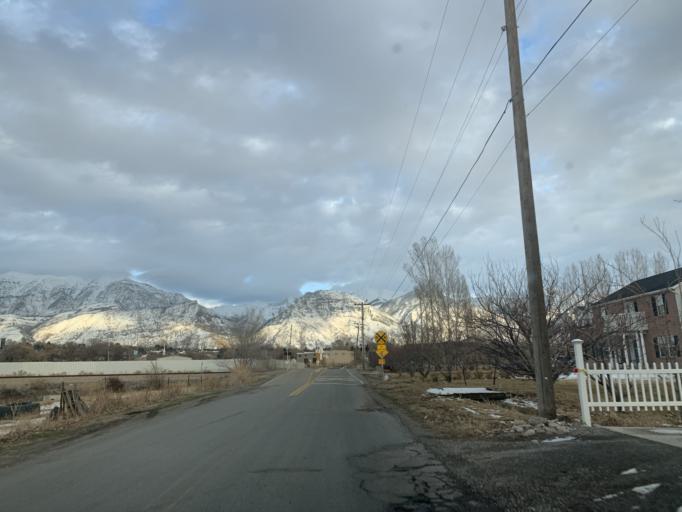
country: US
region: Utah
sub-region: Utah County
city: Orem
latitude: 40.2561
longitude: -111.7058
